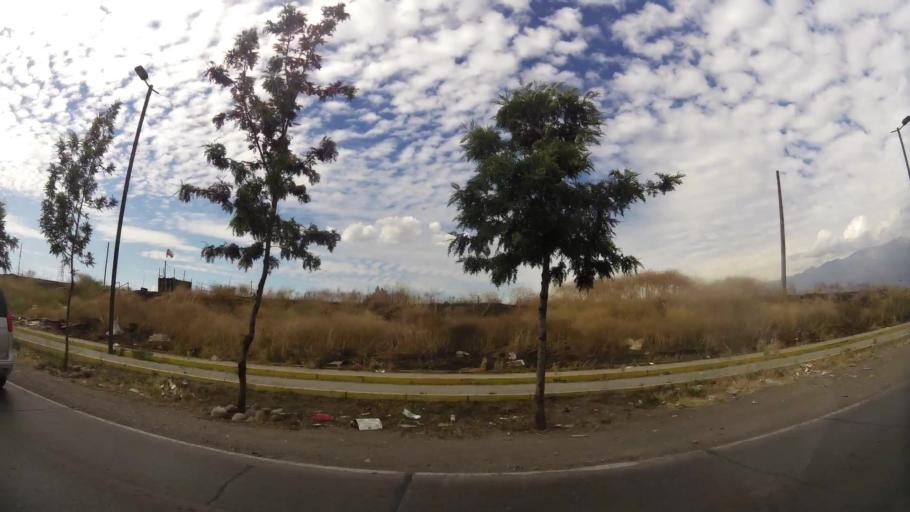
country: CL
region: Santiago Metropolitan
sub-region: Provincia de Santiago
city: La Pintana
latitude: -33.5771
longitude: -70.6311
